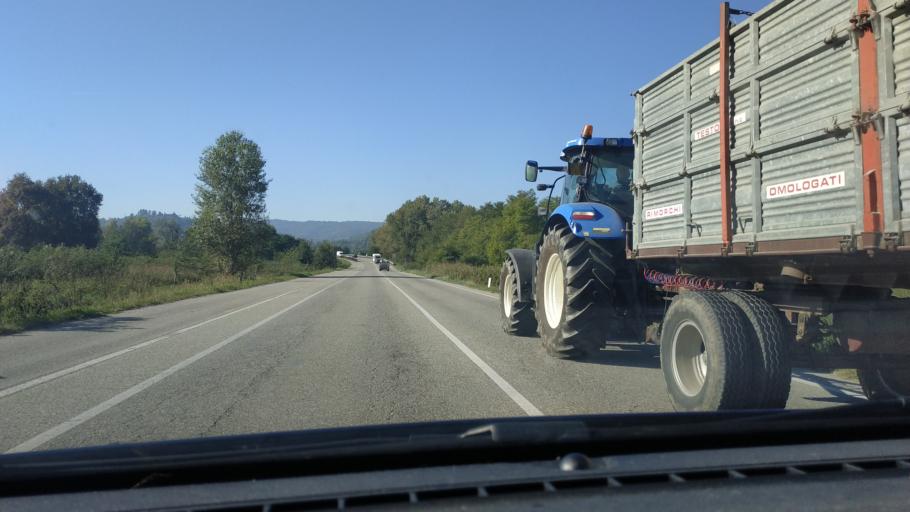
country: IT
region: Piedmont
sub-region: Provincia di Torino
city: San Sebastiano da Po
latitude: 45.1765
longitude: 7.9455
